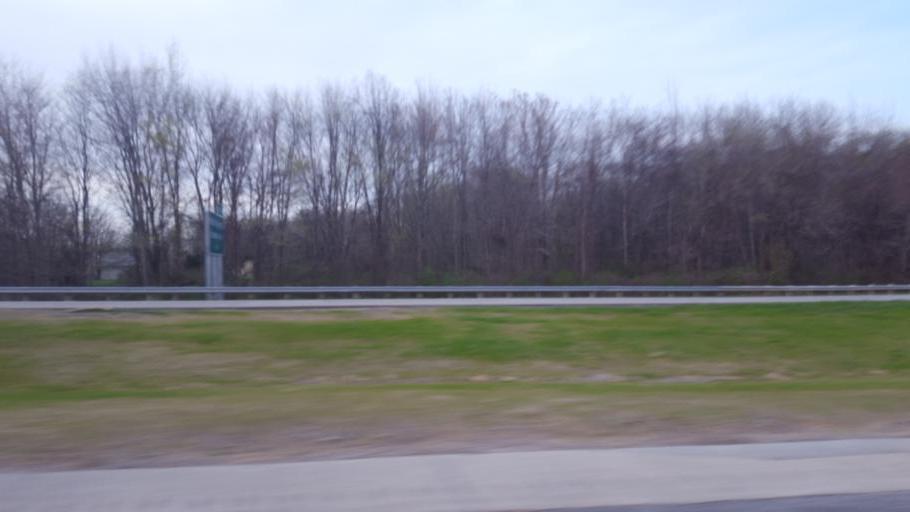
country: US
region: Ohio
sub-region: Lorain County
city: Sheffield
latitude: 41.4053
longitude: -82.1477
